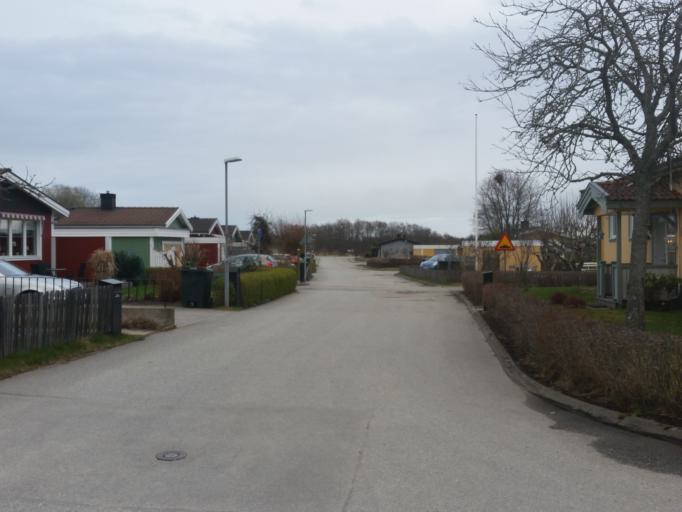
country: SE
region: Stockholm
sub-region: Sodertalje Kommun
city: Pershagen
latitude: 59.0857
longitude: 17.5677
